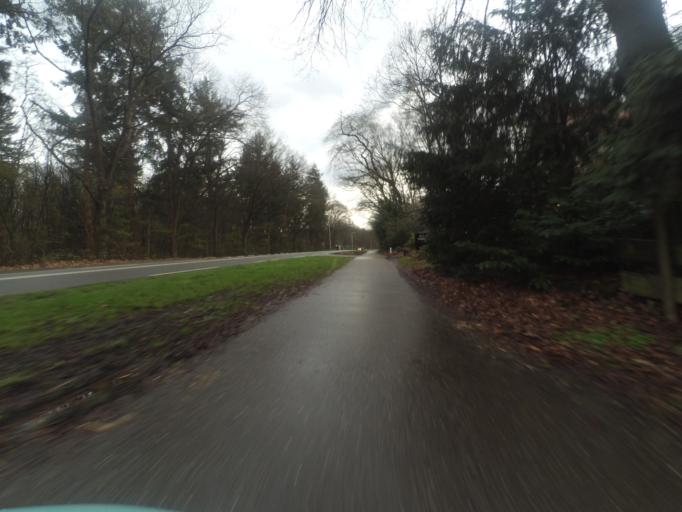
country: NL
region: Gelderland
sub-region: Gemeente Apeldoorn
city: Beekbergen
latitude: 52.1517
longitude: 5.9603
